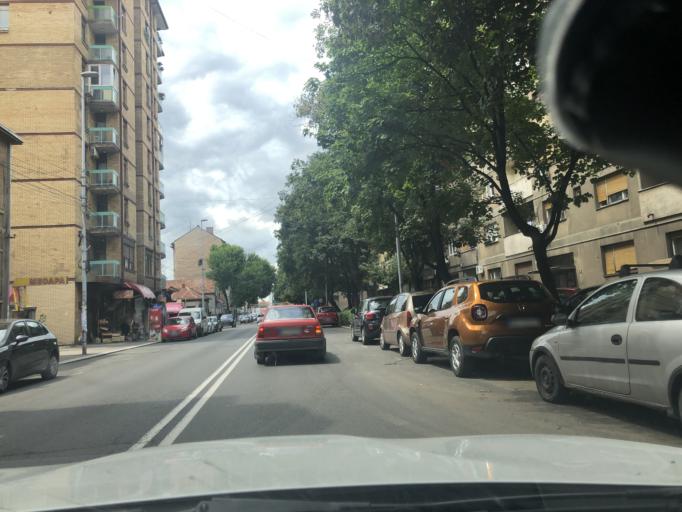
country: RS
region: Central Serbia
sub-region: Nisavski Okrug
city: Nis
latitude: 43.3179
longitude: 21.8895
